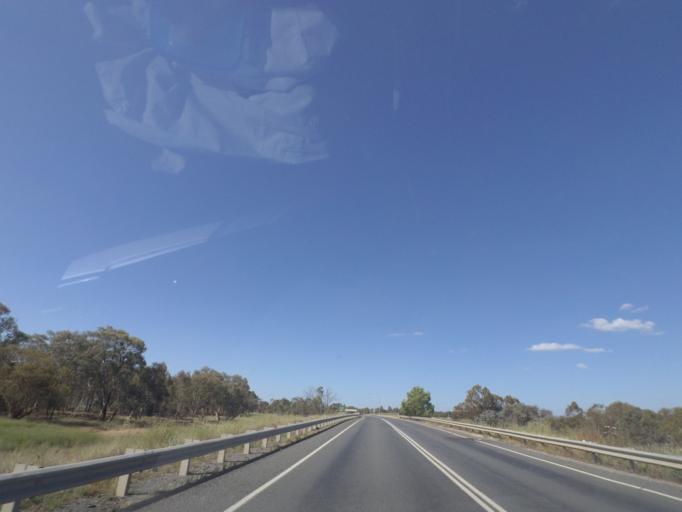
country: AU
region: New South Wales
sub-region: Albury Municipality
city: Lavington
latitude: -36.0031
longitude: 146.9884
